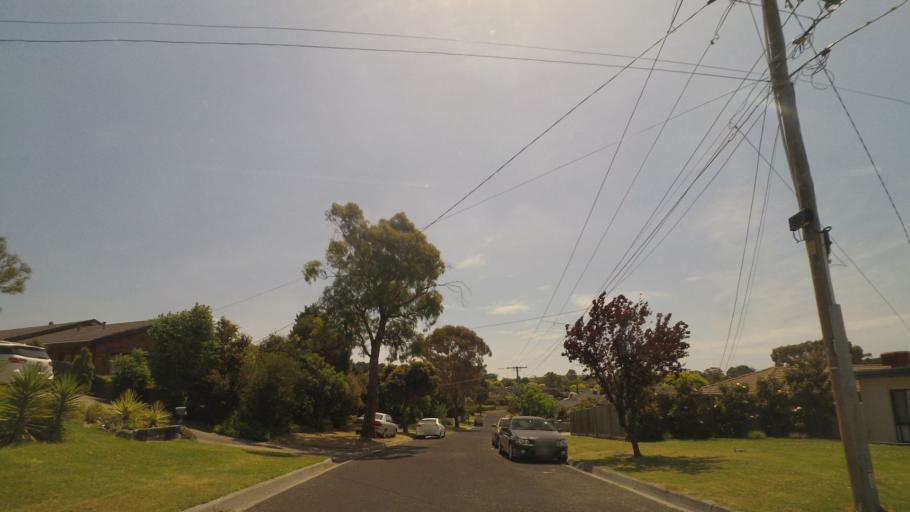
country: AU
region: Victoria
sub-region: Yarra Ranges
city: Chirnside Park
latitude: -37.7547
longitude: 145.3091
